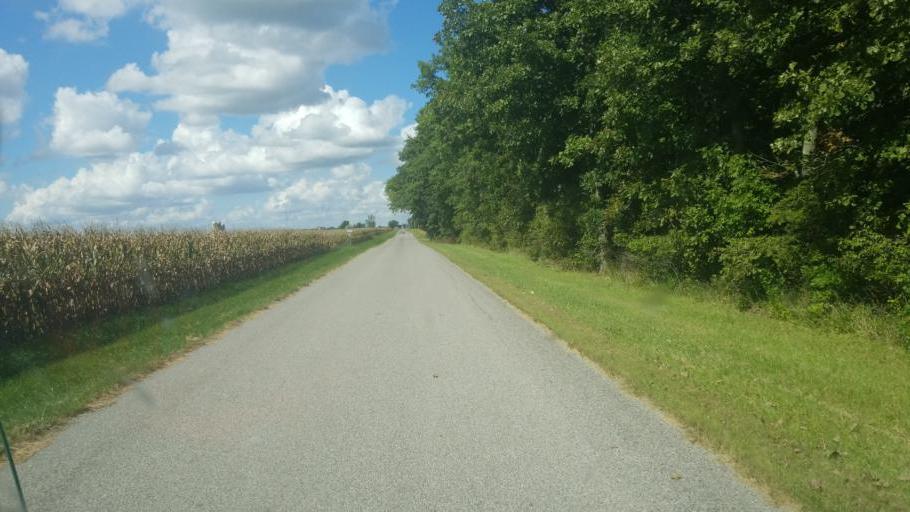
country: US
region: Ohio
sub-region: Hardin County
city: Kenton
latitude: 40.5099
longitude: -83.5393
